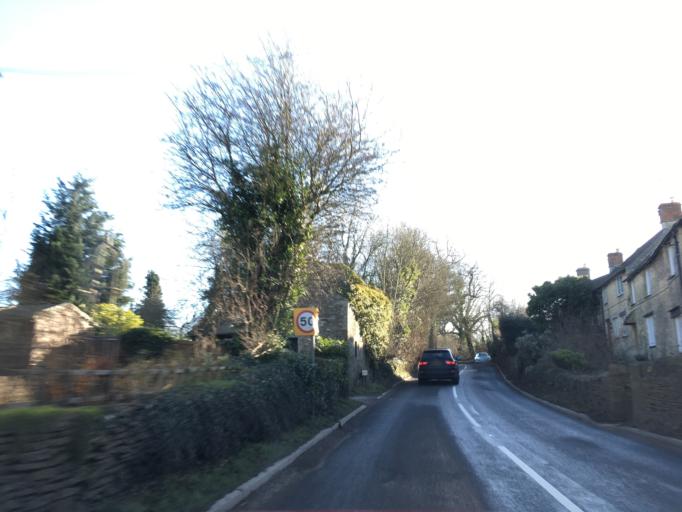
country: GB
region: England
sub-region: Wiltshire
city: Biddestone
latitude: 51.4915
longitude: -2.1996
